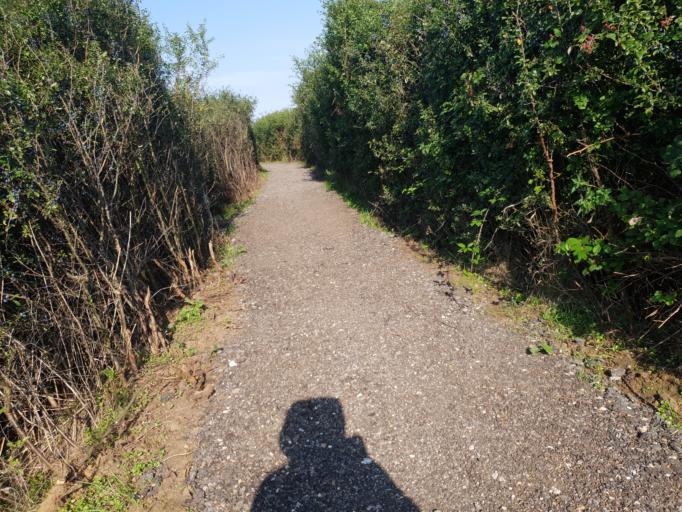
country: GB
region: England
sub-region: Suffolk
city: East Bergholt
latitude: 51.9535
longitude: 1.0308
